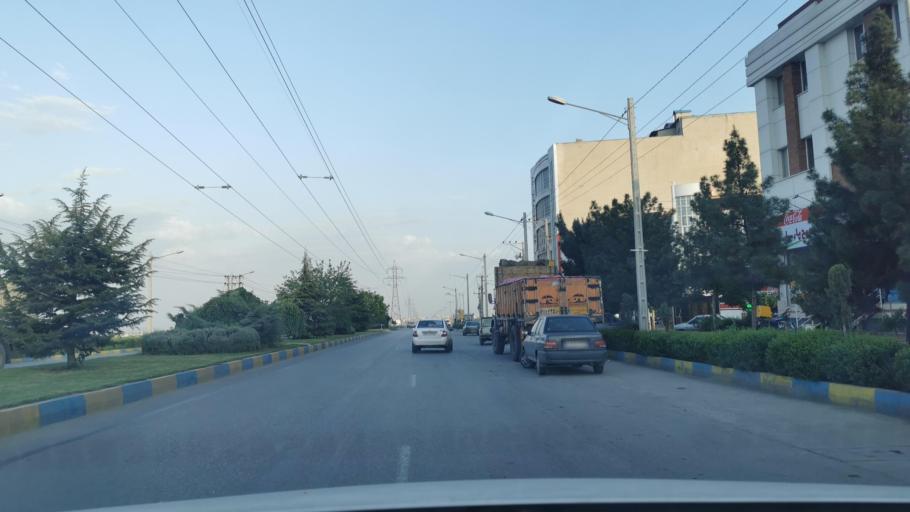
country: IR
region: Razavi Khorasan
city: Torqabeh
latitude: 36.4230
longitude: 59.4259
